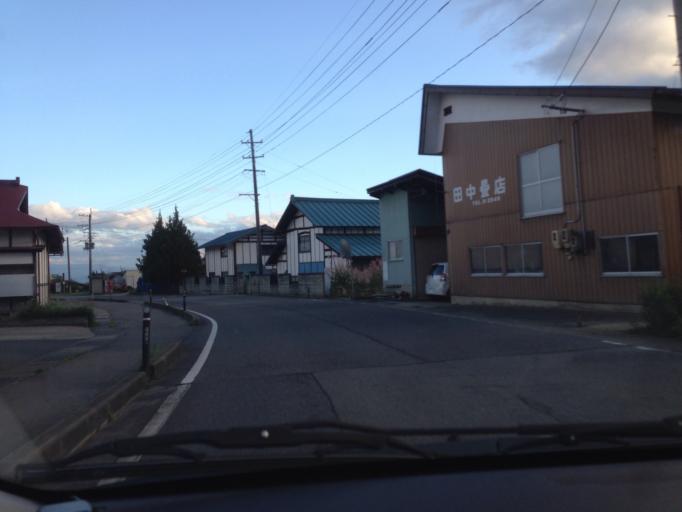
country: JP
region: Fukushima
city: Kitakata
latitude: 37.6962
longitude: 139.8569
